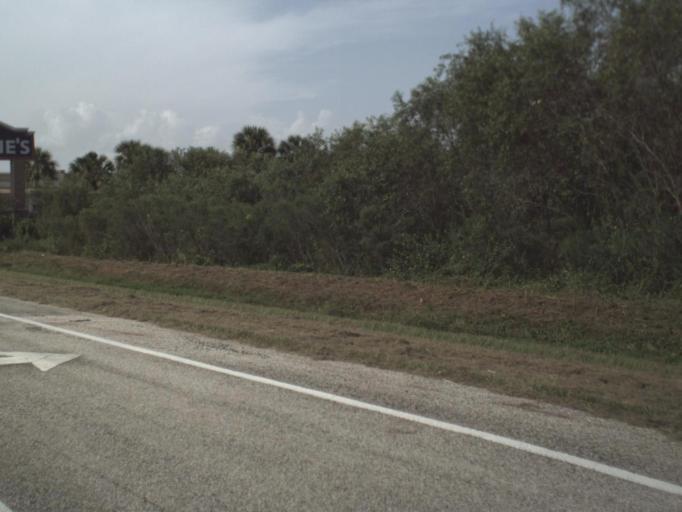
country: US
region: Florida
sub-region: Polk County
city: Lake Wales
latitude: 27.9468
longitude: -81.6164
